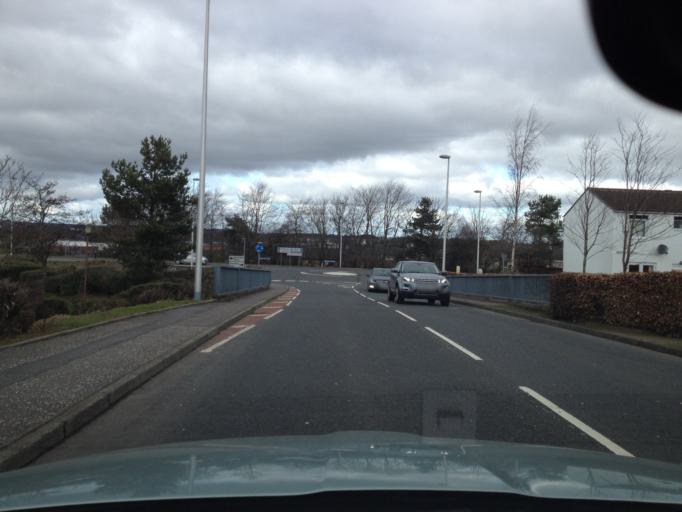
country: GB
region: Scotland
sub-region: West Lothian
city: Livingston
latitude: 55.8774
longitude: -3.5114
